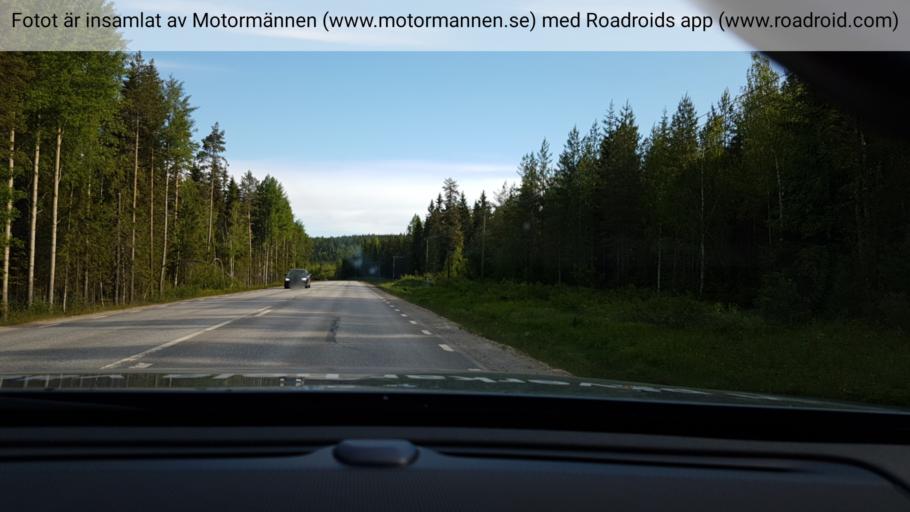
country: SE
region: Vaesterbotten
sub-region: Vannas Kommun
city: Vaennaes
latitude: 63.9356
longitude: 19.7711
